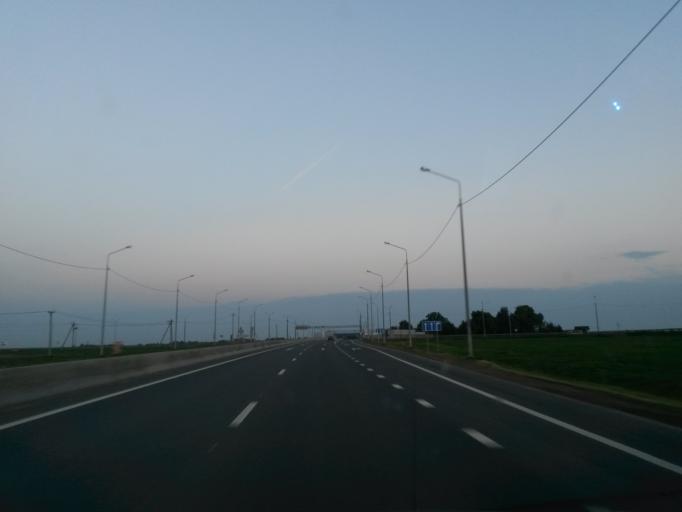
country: RU
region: Jaroslavl
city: Yaroslavl
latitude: 57.7229
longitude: 39.9010
